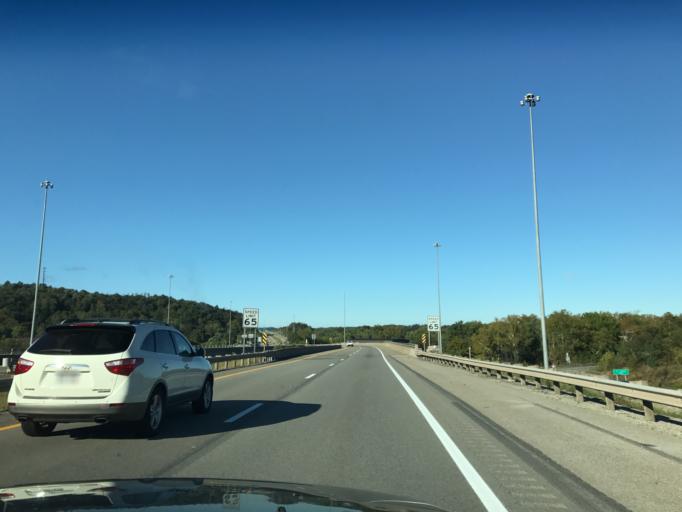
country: US
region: West Virginia
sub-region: Wood County
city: Parkersburg
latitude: 39.2666
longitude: -81.5096
